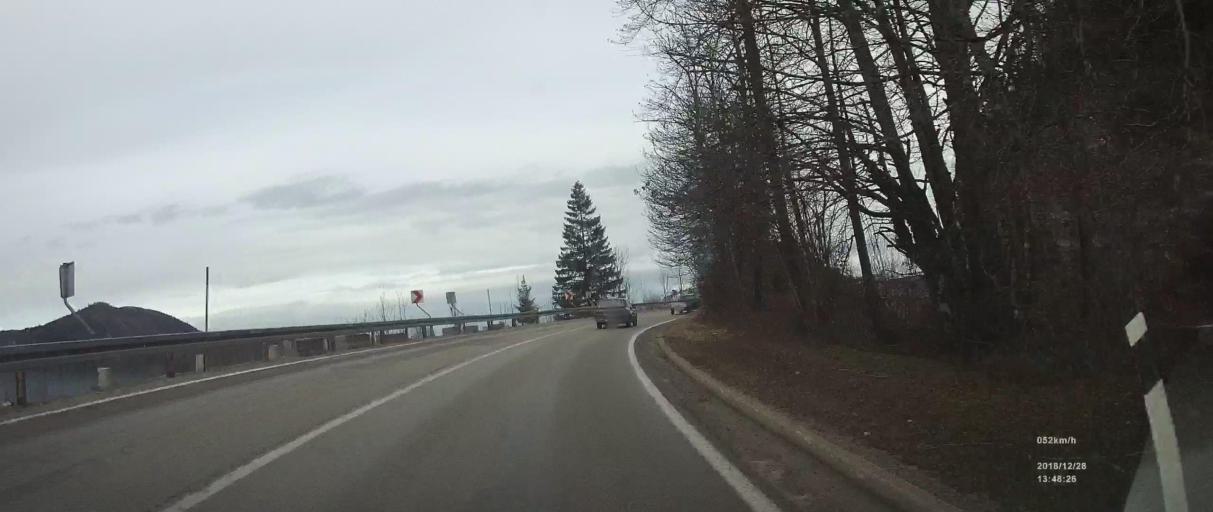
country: HR
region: Primorsko-Goranska
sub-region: Grad Delnice
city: Delnice
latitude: 45.3969
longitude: 14.8086
